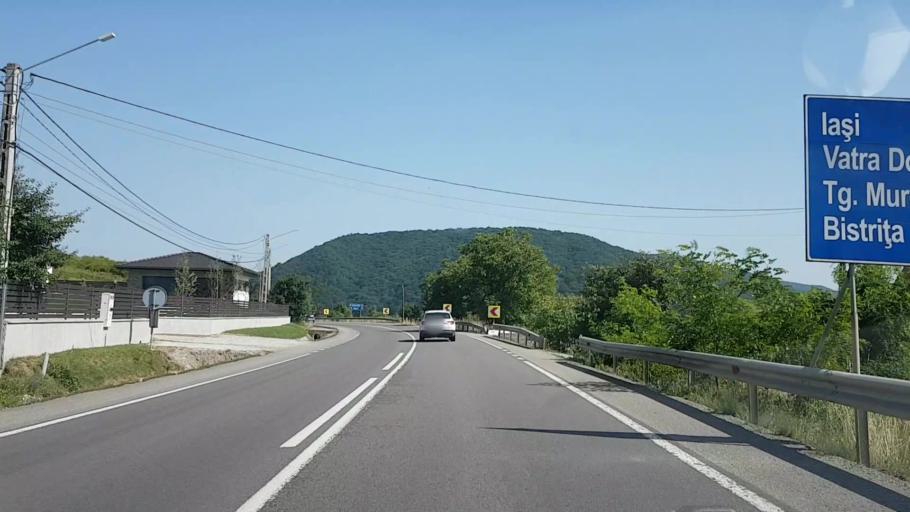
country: RO
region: Bistrita-Nasaud
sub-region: Comuna Sieu-Magherus
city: Sieu-Magherus
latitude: 47.0647
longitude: 24.4137
